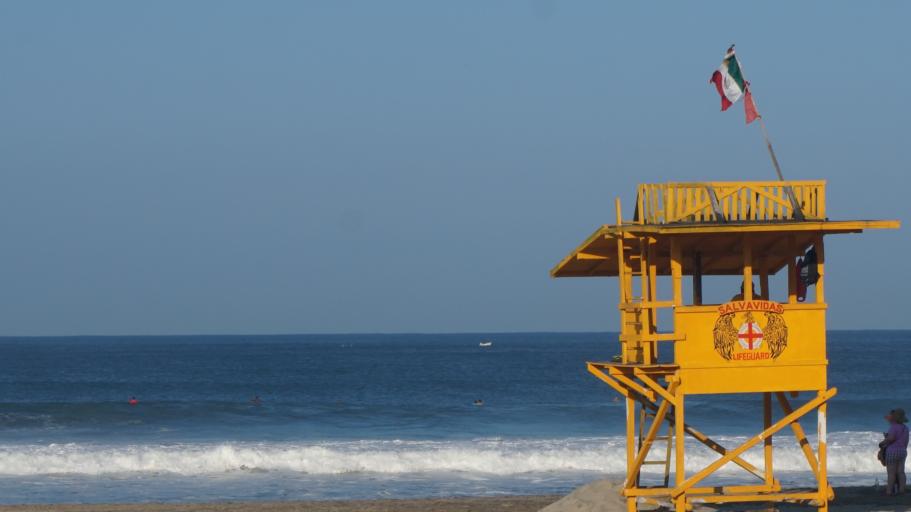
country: MX
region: Oaxaca
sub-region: Santa Maria Colotepec
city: Brisas de Zicatela
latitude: 15.8544
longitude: -97.0559
